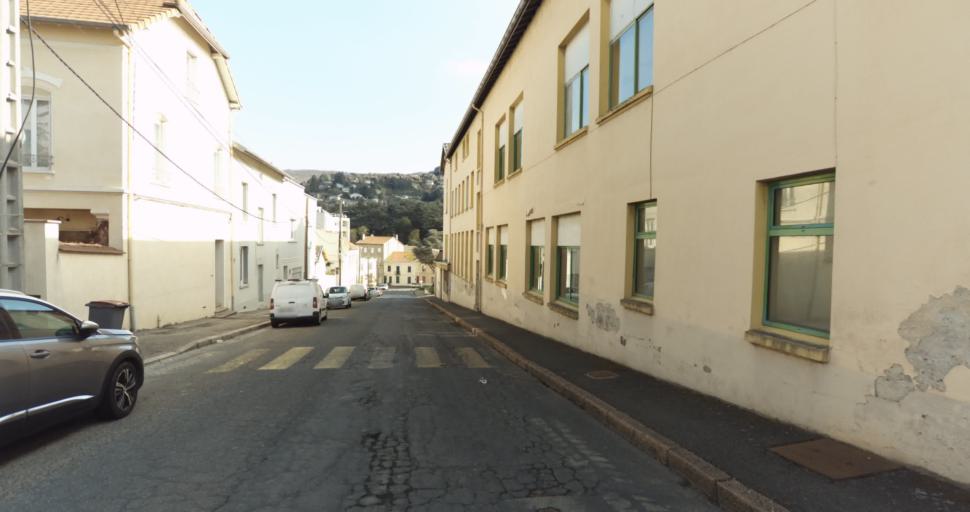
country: FR
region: Rhone-Alpes
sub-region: Departement du Rhone
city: Tarare
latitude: 45.8916
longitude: 4.4374
